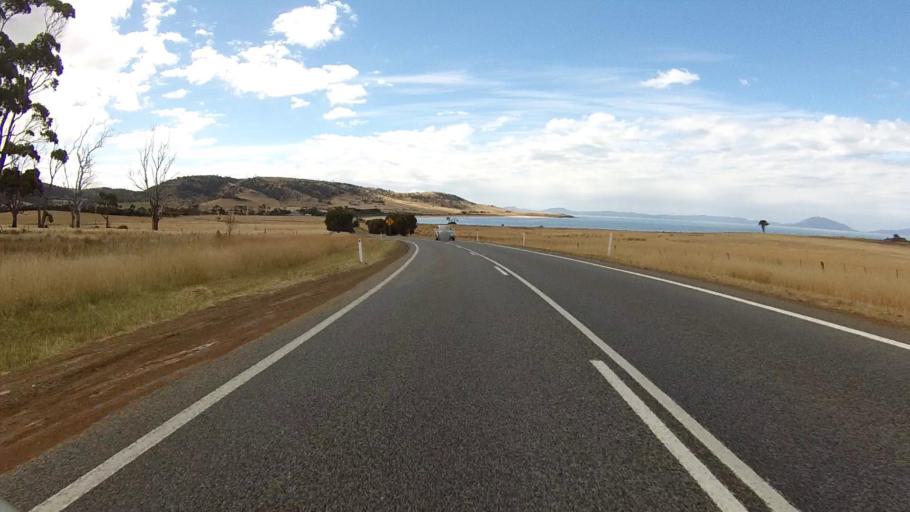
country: AU
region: Tasmania
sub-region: Sorell
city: Sorell
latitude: -42.2110
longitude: 148.0390
